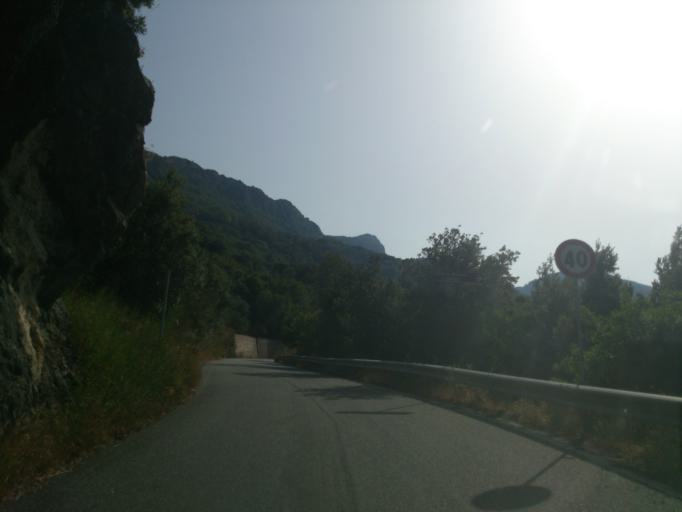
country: IT
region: Calabria
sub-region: Provincia di Reggio Calabria
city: Pazzano
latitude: 38.4719
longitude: 16.4423
